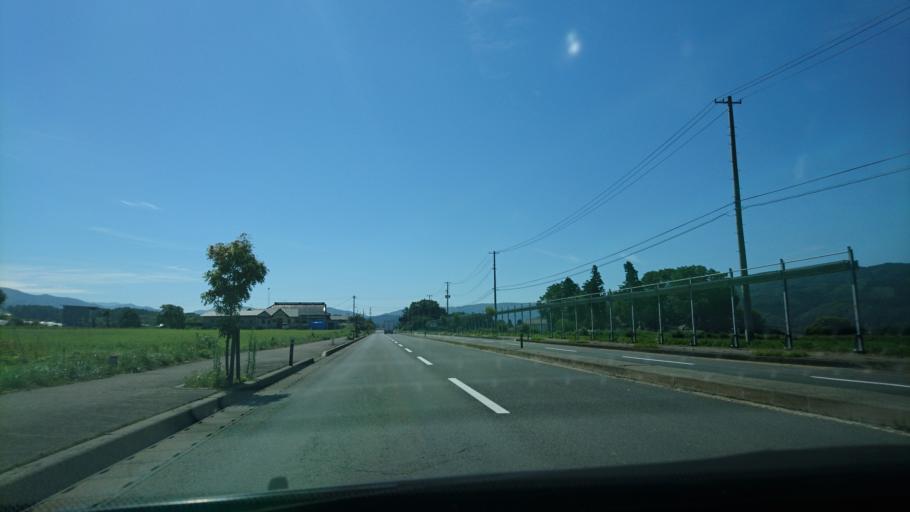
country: JP
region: Iwate
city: Tono
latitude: 39.3218
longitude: 141.5662
